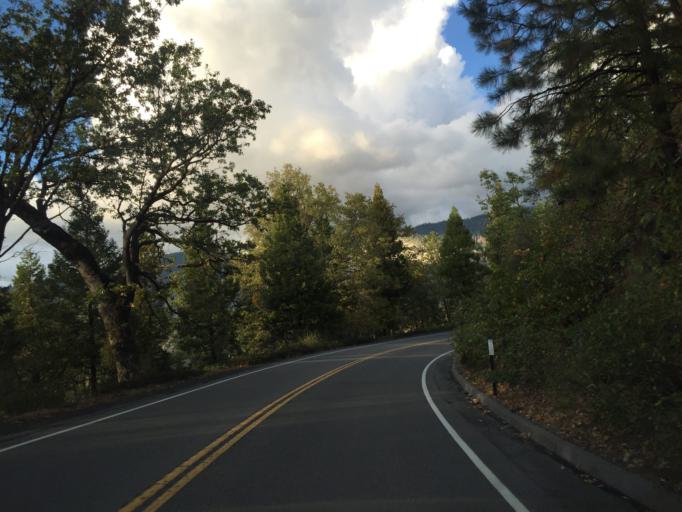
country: US
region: California
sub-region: Madera County
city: Ahwahnee
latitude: 37.5138
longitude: -119.6343
